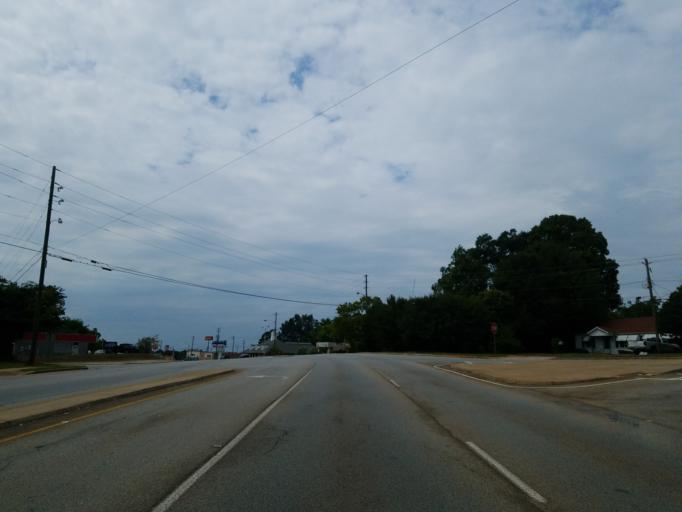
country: US
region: Georgia
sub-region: Spalding County
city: Experiment
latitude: 33.2734
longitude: -84.2876
